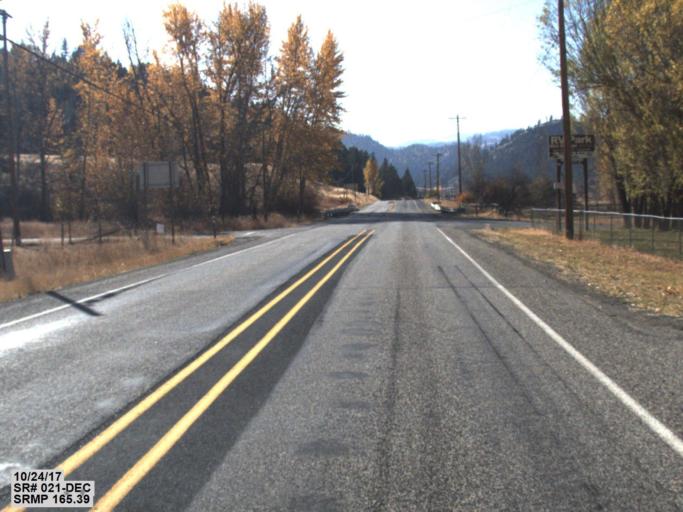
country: US
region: Washington
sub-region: Ferry County
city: Republic
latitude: 48.6793
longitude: -118.6639
